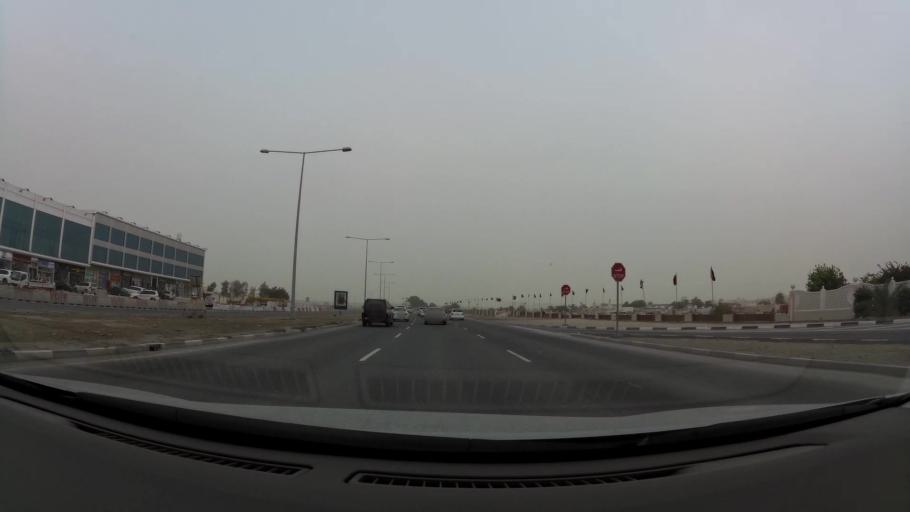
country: QA
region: Baladiyat ad Dawhah
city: Doha
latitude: 25.2274
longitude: 51.4926
